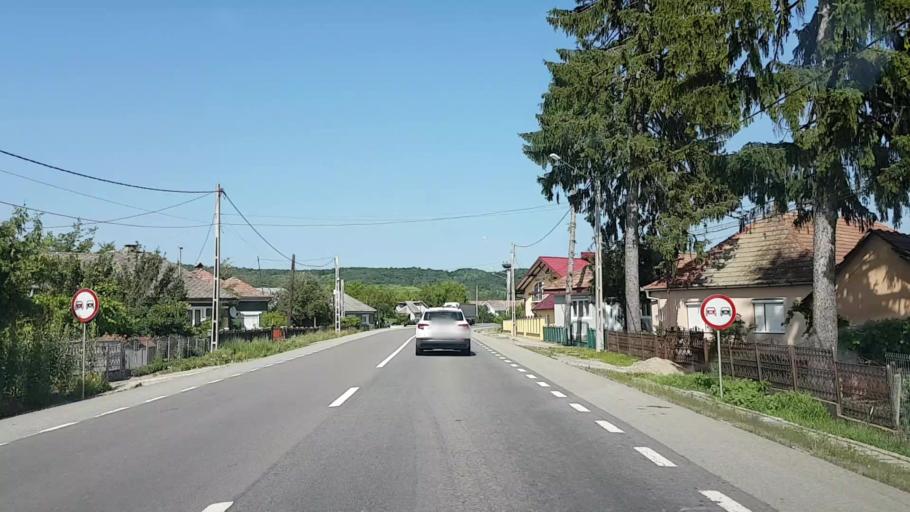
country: RO
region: Bistrita-Nasaud
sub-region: Comuna Sintereag
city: Sintereag
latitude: 47.1801
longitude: 24.2808
